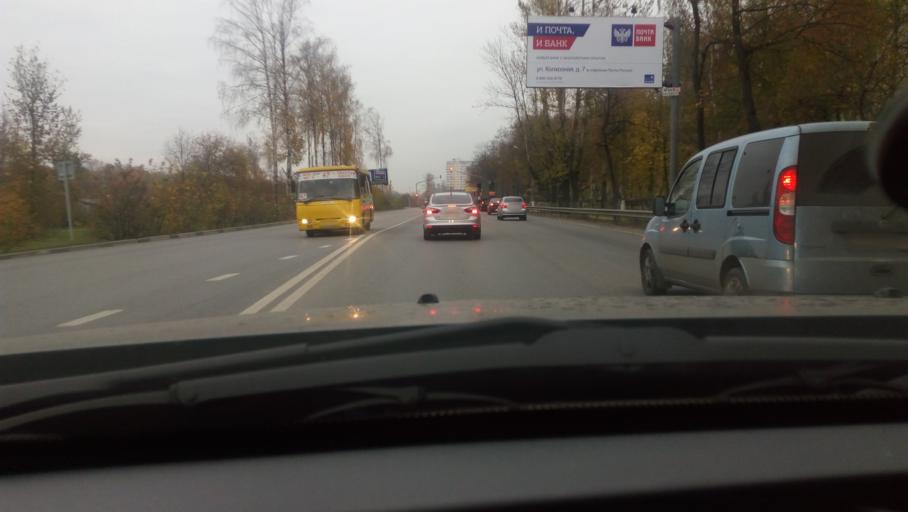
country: RU
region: Moskovskaya
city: Saltykovka
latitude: 55.7509
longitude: 37.9745
